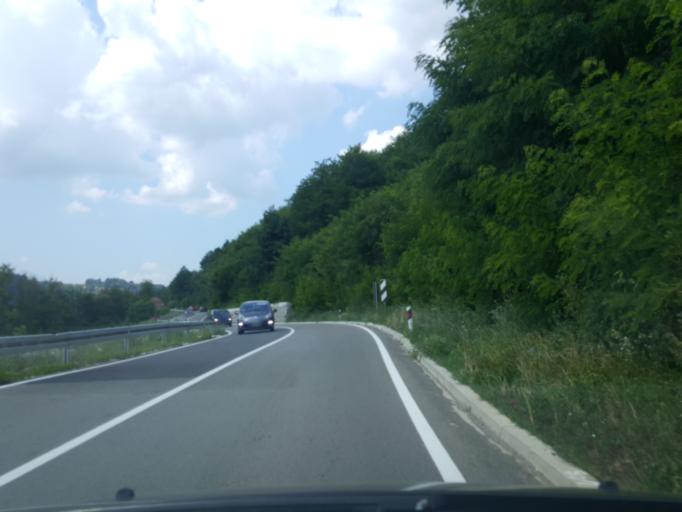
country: RS
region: Central Serbia
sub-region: Sumadijski Okrug
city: Arangelovac
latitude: 44.1903
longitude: 20.5722
